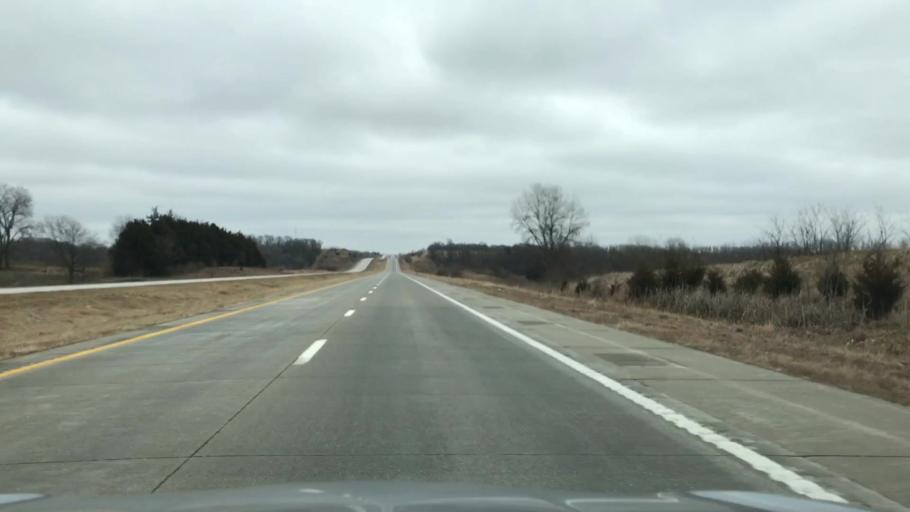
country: US
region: Missouri
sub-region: Caldwell County
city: Hamilton
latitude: 39.7350
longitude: -93.8293
